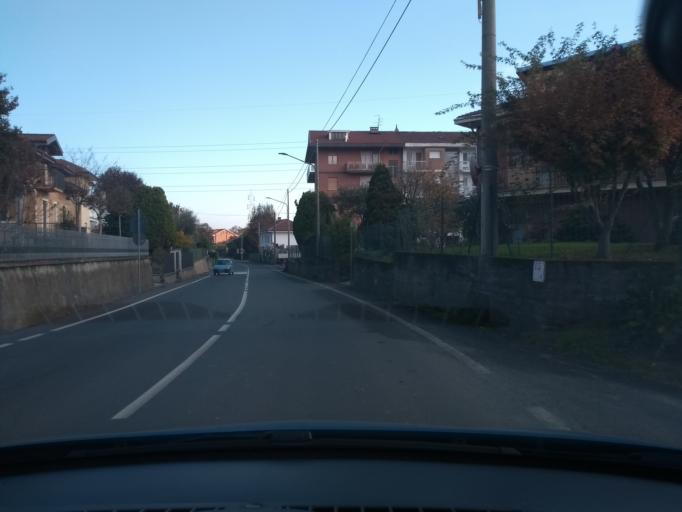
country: IT
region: Piedmont
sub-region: Provincia di Torino
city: Fiano
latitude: 45.2151
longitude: 7.5244
